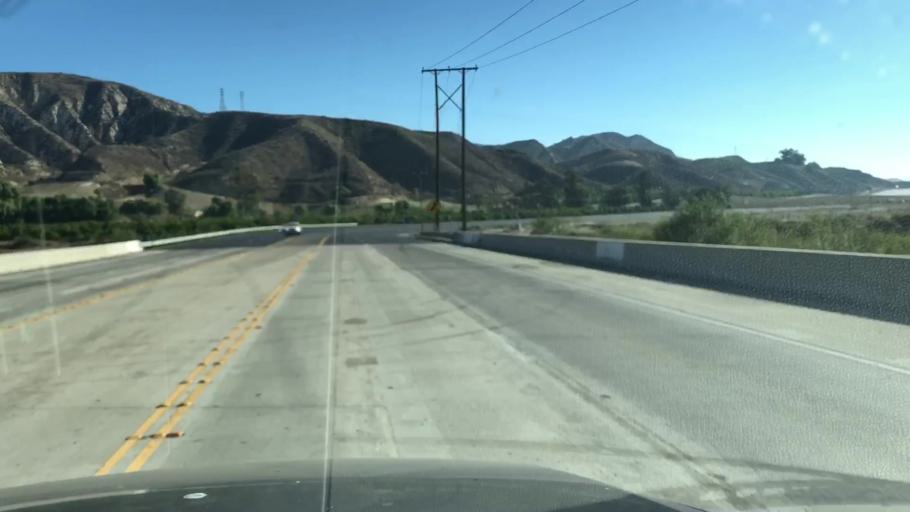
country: US
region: California
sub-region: Ventura County
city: Piru
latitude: 34.4099
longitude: -118.7859
